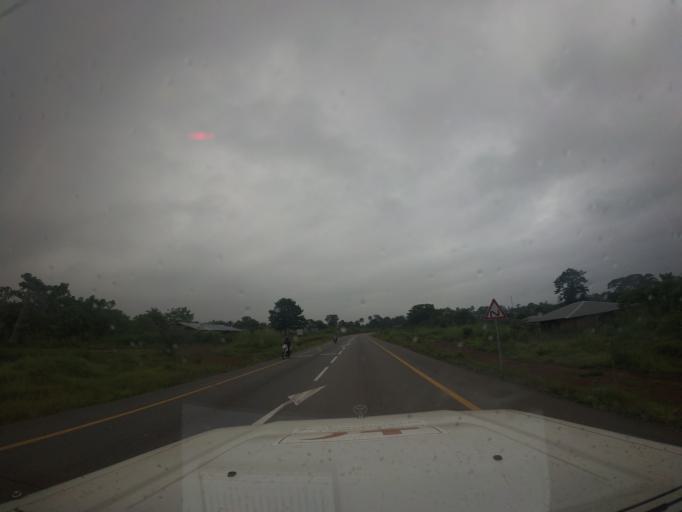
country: SL
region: Eastern Province
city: Hangha
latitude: 7.9340
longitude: -11.1472
